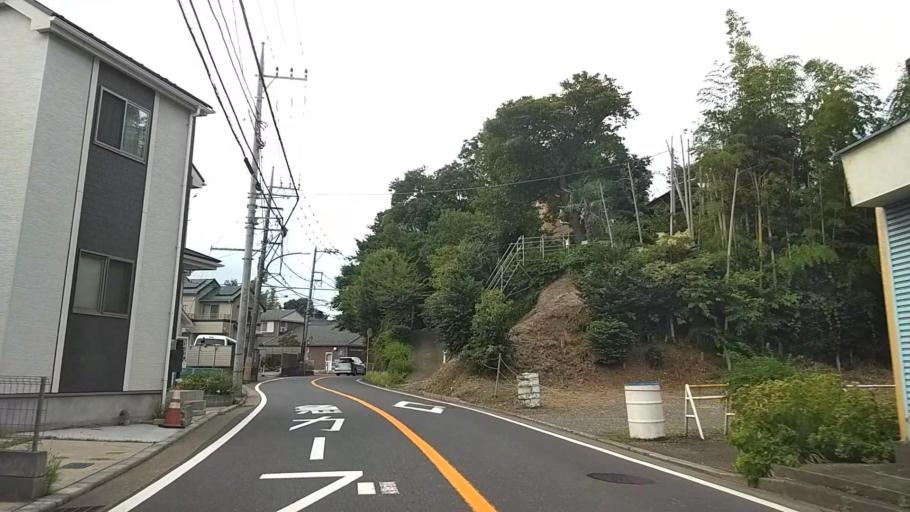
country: JP
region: Kanagawa
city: Yokohama
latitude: 35.4897
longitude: 139.5715
